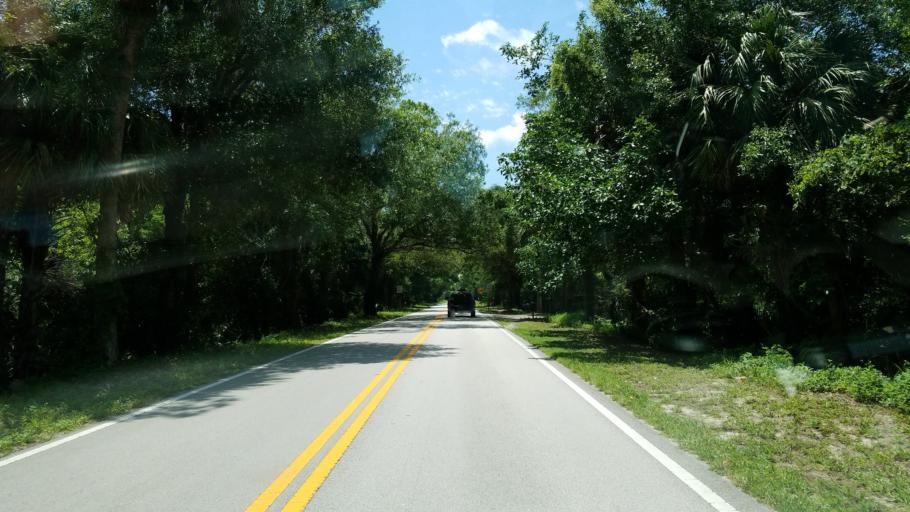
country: US
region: Florida
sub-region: Martin County
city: Indiantown
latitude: 27.1622
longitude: -80.5803
